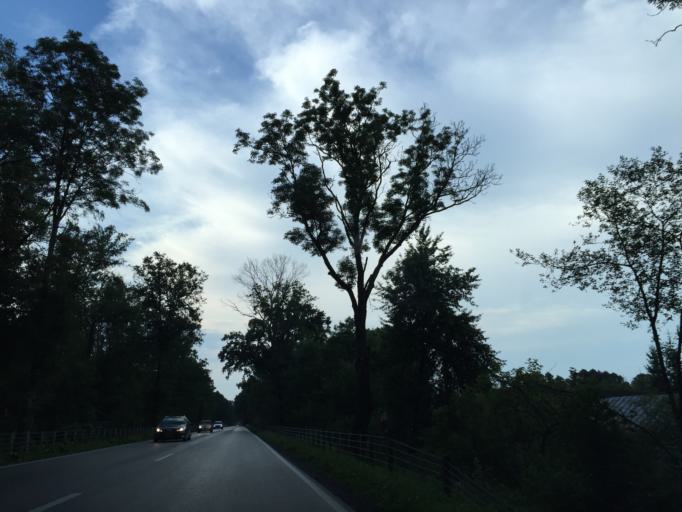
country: PL
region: Masovian Voivodeship
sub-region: Powiat wegrowski
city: Sadowne
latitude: 52.6570
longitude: 21.8476
